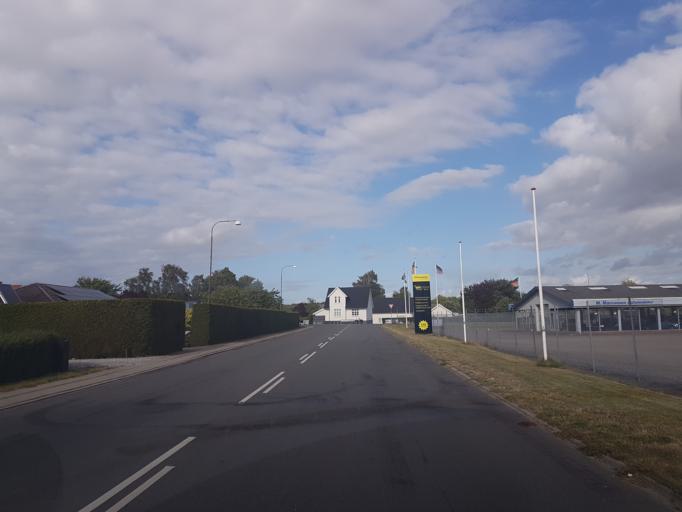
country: DK
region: South Denmark
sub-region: Nordfyns Kommune
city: Bogense
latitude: 55.5559
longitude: 10.0862
